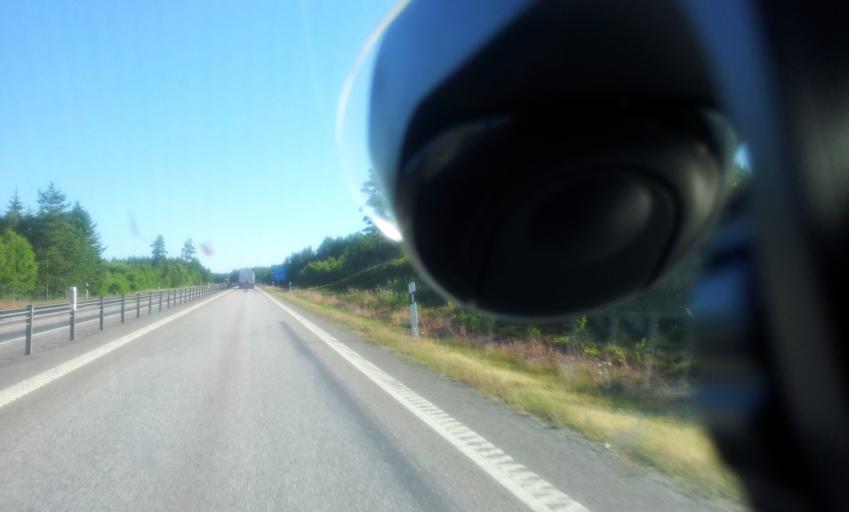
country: SE
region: Kalmar
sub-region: Torsas Kommun
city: Torsas
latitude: 56.4866
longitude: 16.0835
